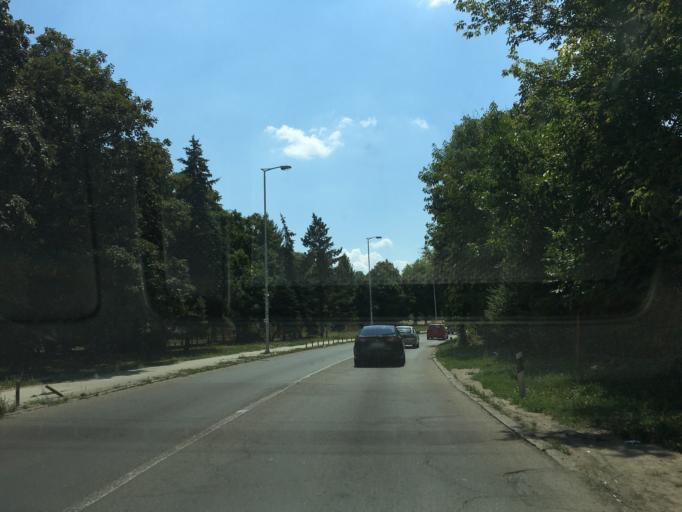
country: RS
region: Central Serbia
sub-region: Belgrade
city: Mladenovac
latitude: 44.4497
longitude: 20.6856
